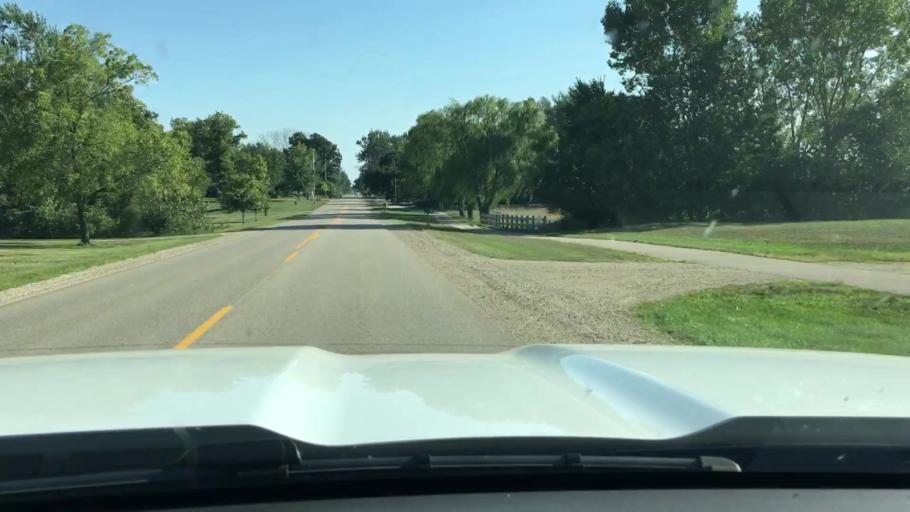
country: US
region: Michigan
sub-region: Ottawa County
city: Zeeland
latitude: 42.7873
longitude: -85.9404
